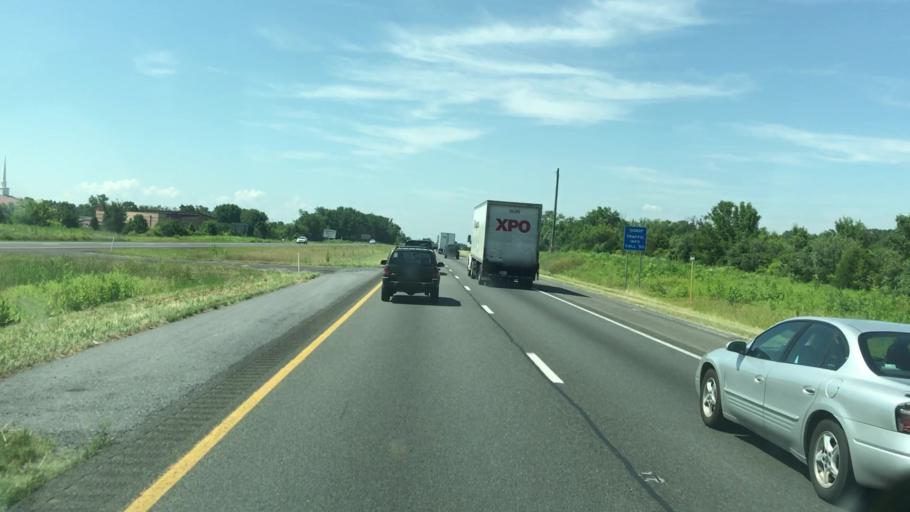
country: US
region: Virginia
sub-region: Frederick County
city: Stephens City
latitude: 39.0951
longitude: -78.2066
